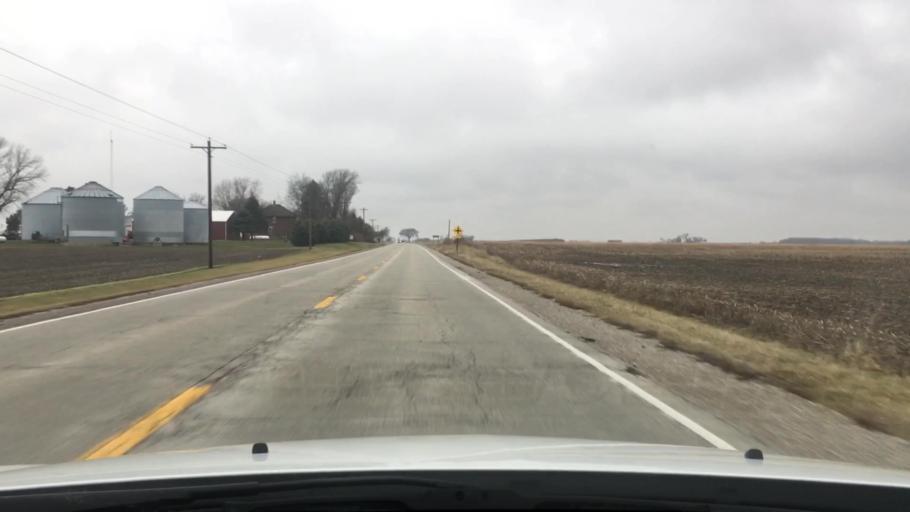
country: US
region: Illinois
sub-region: Iroquois County
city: Clifton
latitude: 40.8877
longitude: -87.8436
